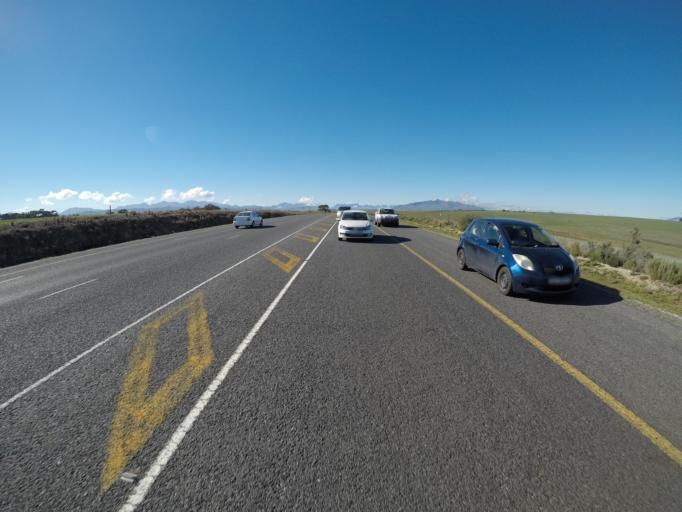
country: ZA
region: Western Cape
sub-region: Overberg District Municipality
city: Caledon
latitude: -34.2242
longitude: 19.2775
